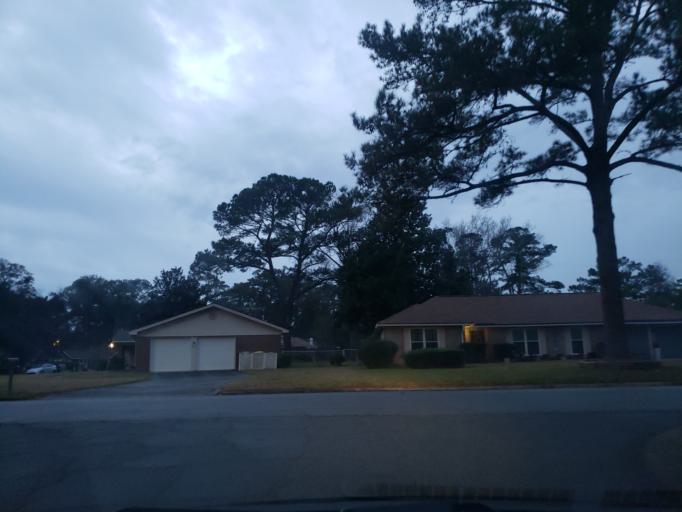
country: US
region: Georgia
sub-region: Chatham County
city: Montgomery
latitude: 31.9927
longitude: -81.1495
